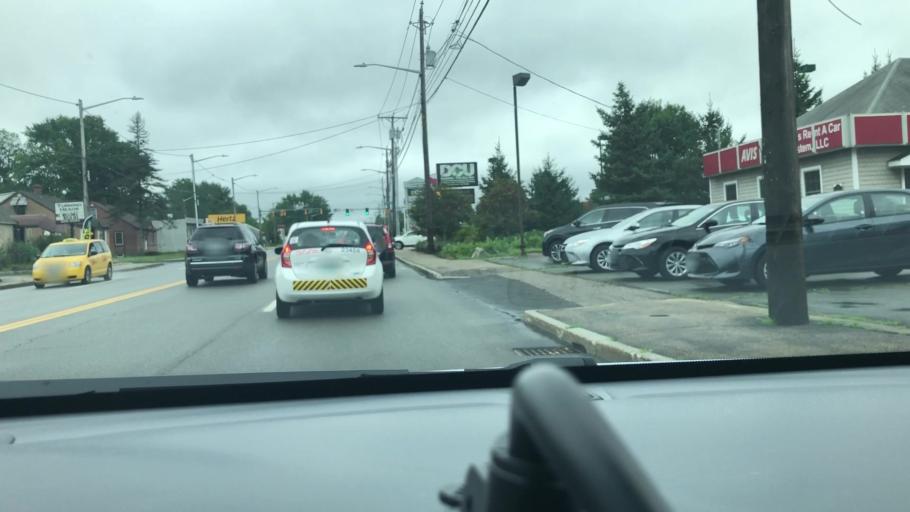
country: US
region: New Hampshire
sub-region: Hillsborough County
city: Manchester
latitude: 42.9687
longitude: -71.4525
